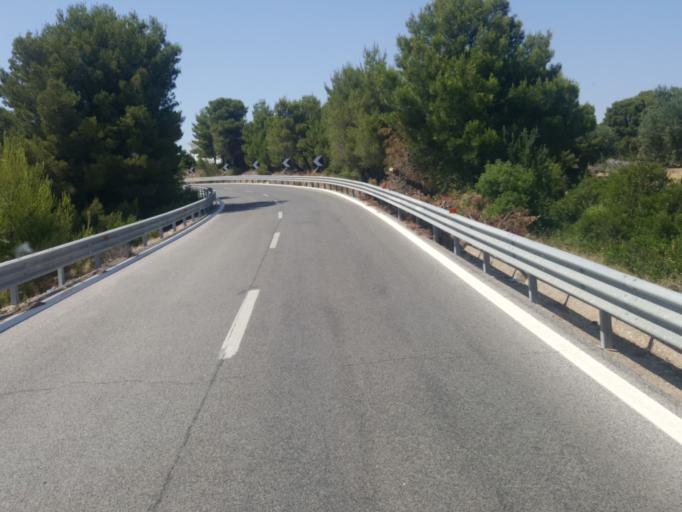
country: IT
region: Apulia
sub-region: Provincia di Taranto
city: Massafra
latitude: 40.5967
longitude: 17.0861
